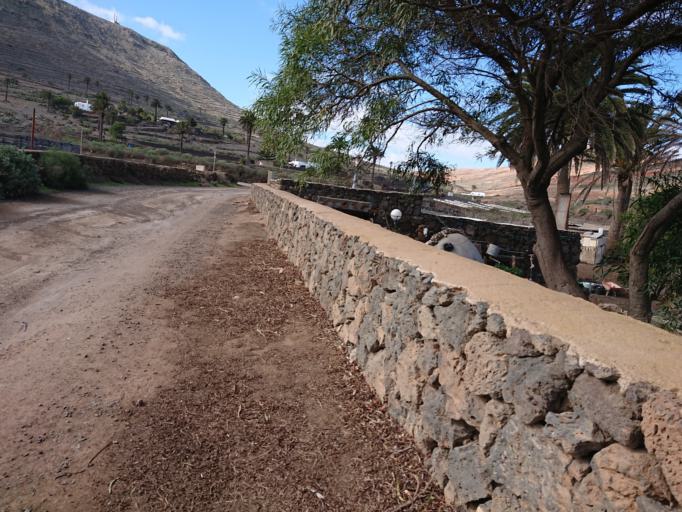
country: ES
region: Canary Islands
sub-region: Provincia de Las Palmas
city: Haria
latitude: 29.1438
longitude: -13.5077
